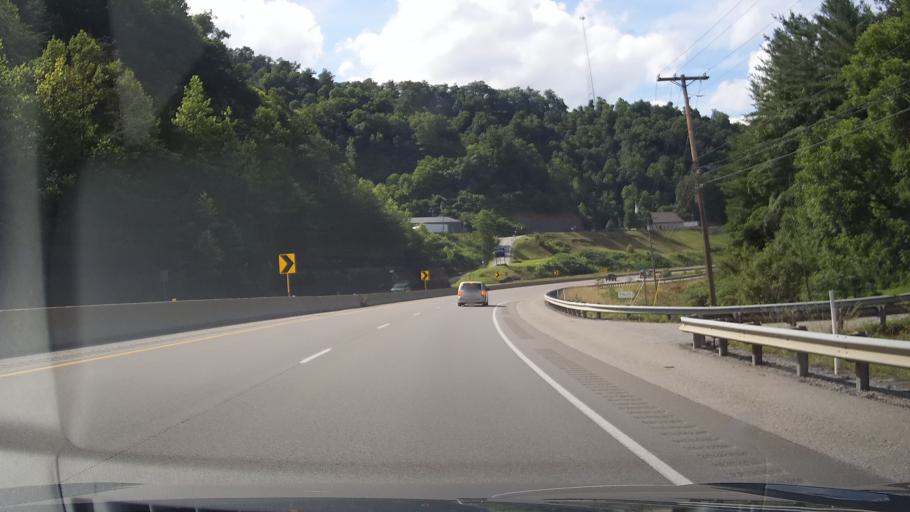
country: US
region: Kentucky
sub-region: Floyd County
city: Prestonsburg
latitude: 37.6496
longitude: -82.7842
